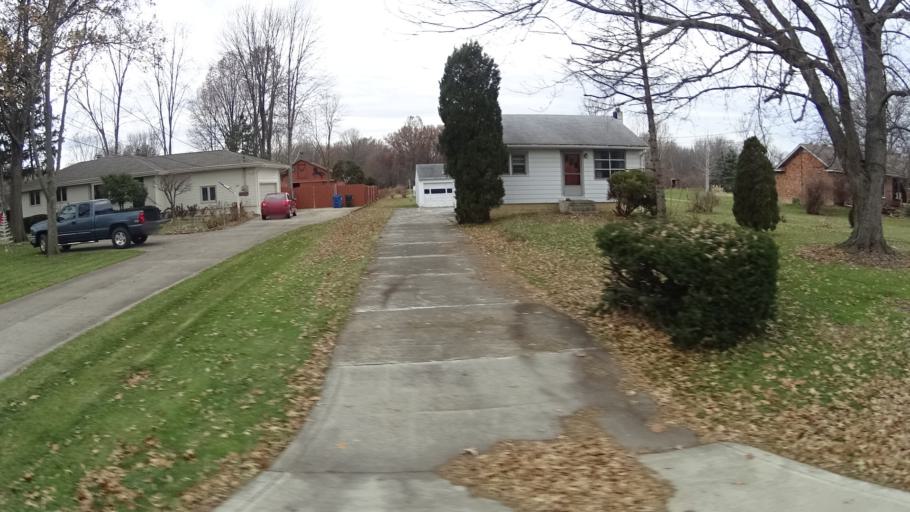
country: US
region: Ohio
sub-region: Cuyahoga County
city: Berea
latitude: 41.3410
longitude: -81.8771
